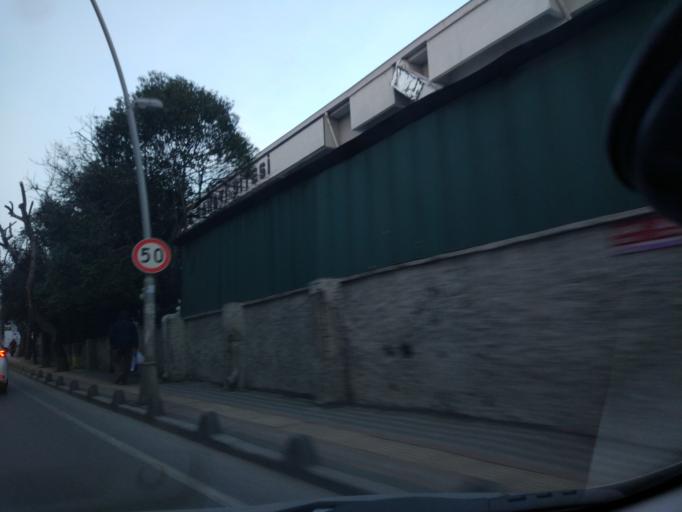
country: TR
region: Istanbul
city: Bahcelievler
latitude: 41.0074
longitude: 28.8220
